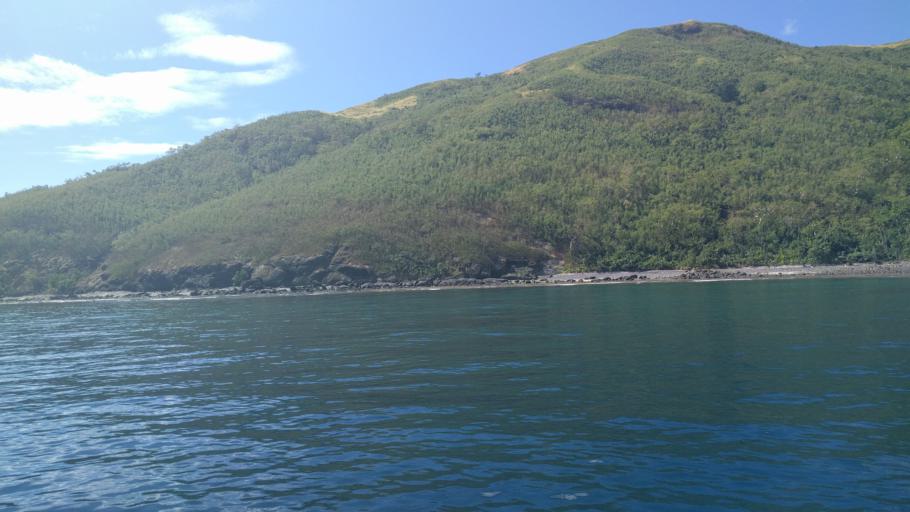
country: FJ
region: Western
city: Lautoka
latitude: -17.2837
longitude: 177.1030
